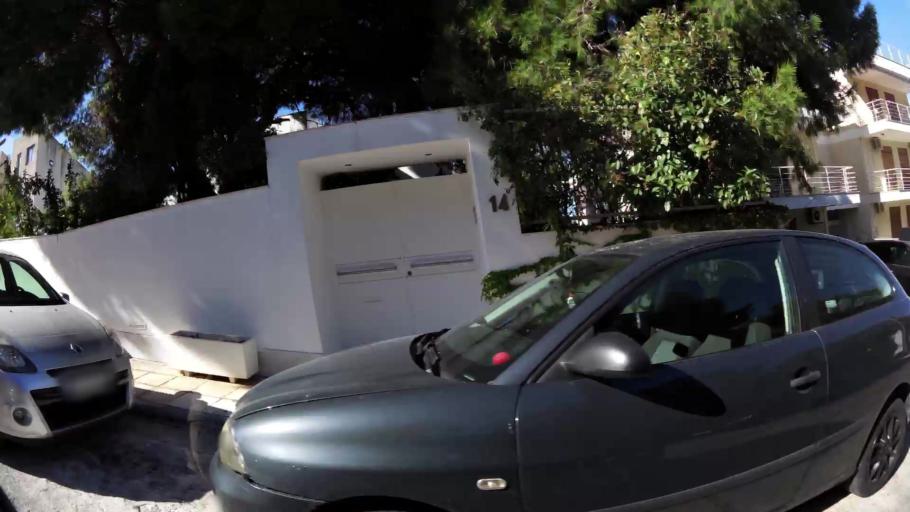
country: GR
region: Attica
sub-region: Nomarchia Anatolikis Attikis
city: Vouliagmeni
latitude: 37.8128
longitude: 23.7854
